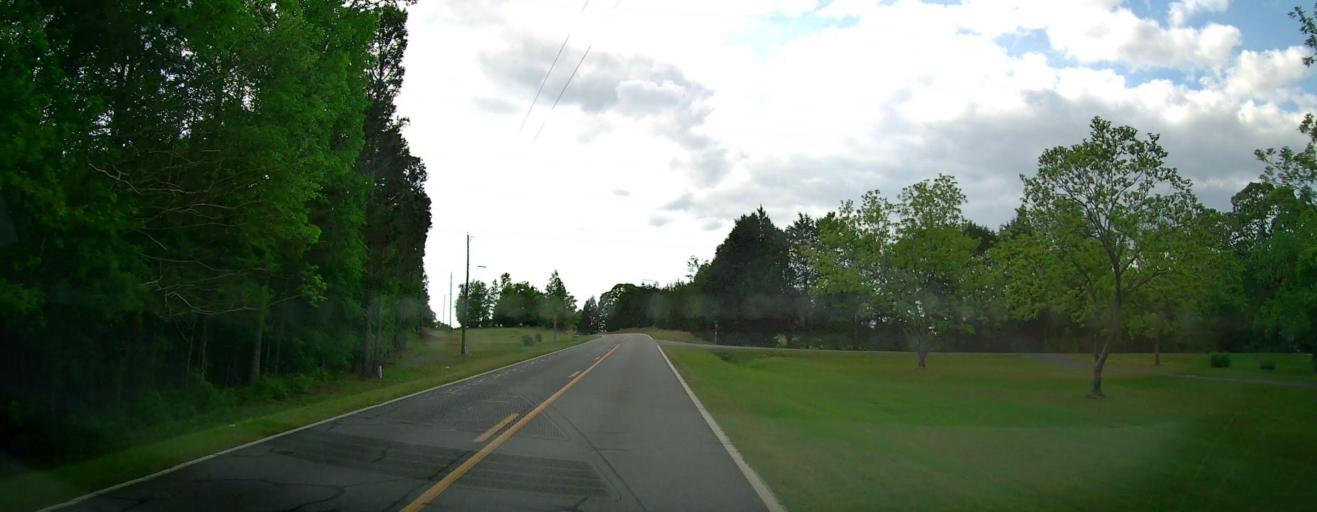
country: US
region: Georgia
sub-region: Baldwin County
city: Hardwick
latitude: 33.0617
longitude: -83.1362
